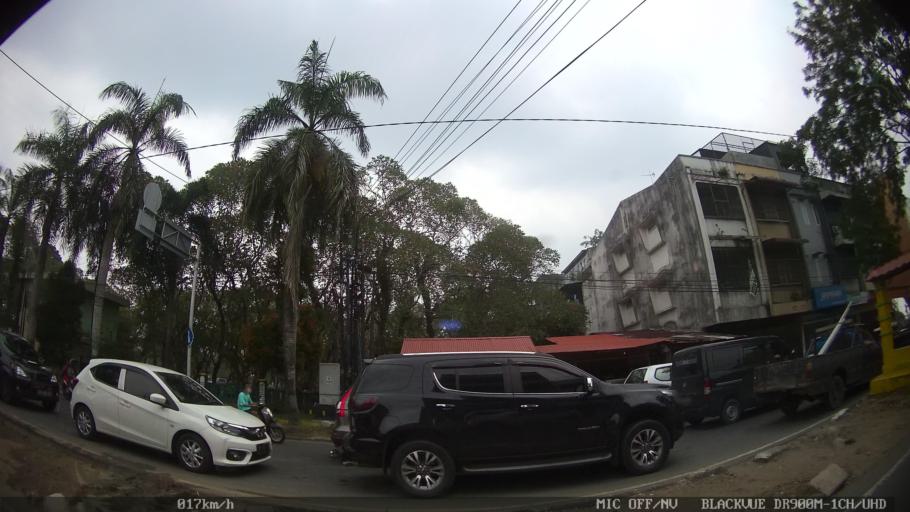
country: ID
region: North Sumatra
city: Medan
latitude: 3.5720
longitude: 98.6858
